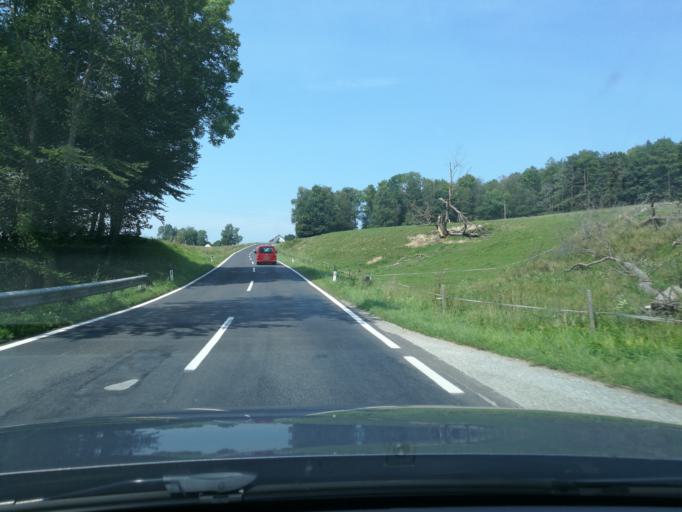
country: DE
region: Bavaria
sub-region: Lower Bavaria
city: Obernzell
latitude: 48.3647
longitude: 13.6690
